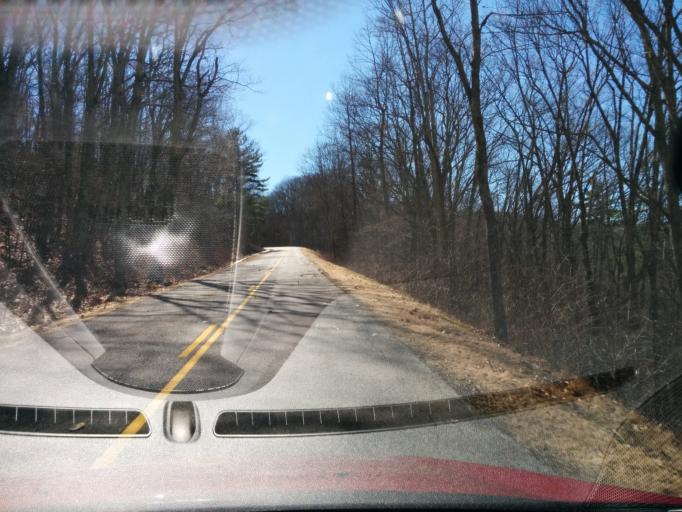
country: US
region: Virginia
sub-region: Augusta County
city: Stuarts Draft
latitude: 37.8815
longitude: -79.1577
